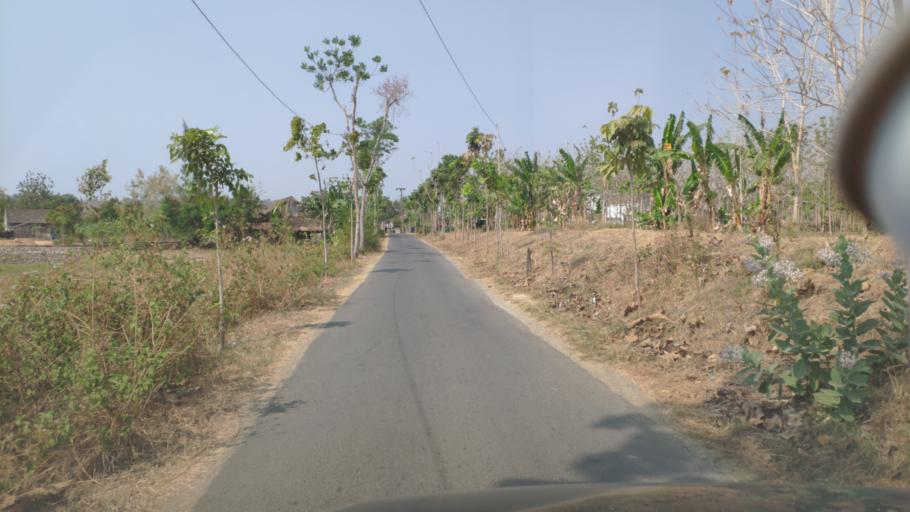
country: ID
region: Central Java
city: Ngadipurwo
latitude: -6.9159
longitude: 111.4544
